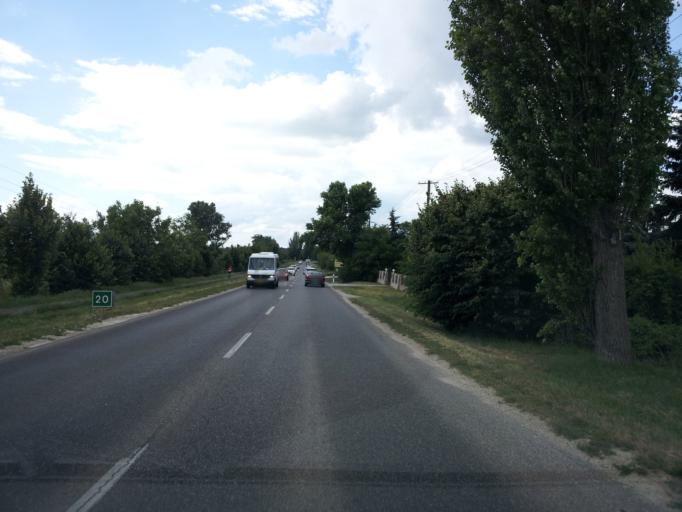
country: HU
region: Veszprem
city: Balatonalmadi
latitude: 47.0579
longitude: 18.0222
